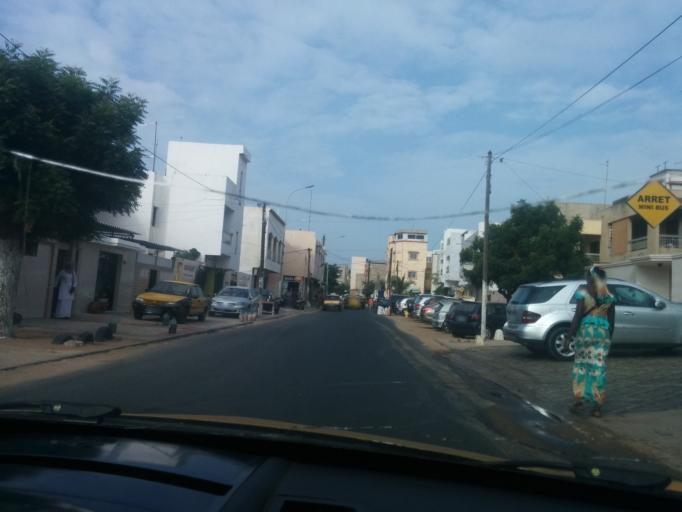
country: SN
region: Dakar
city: Grand Dakar
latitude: 14.7181
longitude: -17.4418
